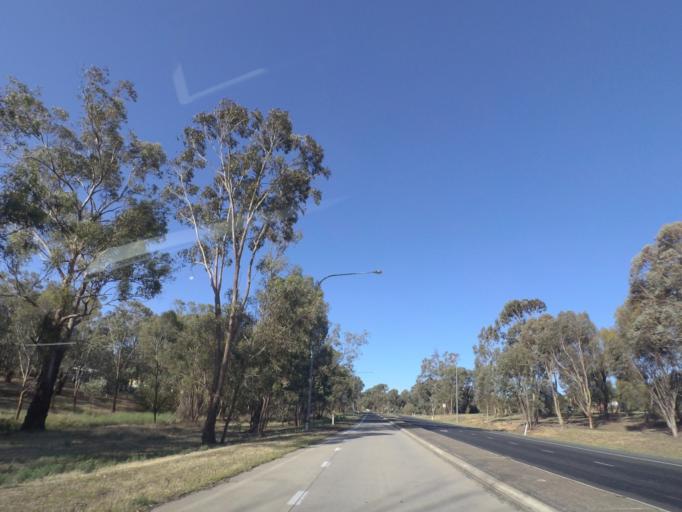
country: AU
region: New South Wales
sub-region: Wagga Wagga
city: Forest Hill
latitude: -35.2748
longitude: 147.7401
